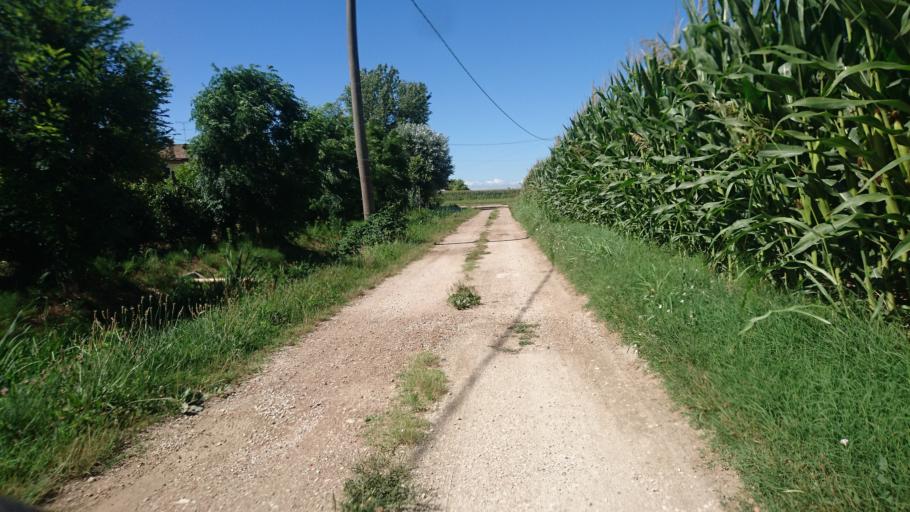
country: IT
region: Veneto
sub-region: Provincia di Padova
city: Campagnola
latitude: 45.2822
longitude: 12.0190
